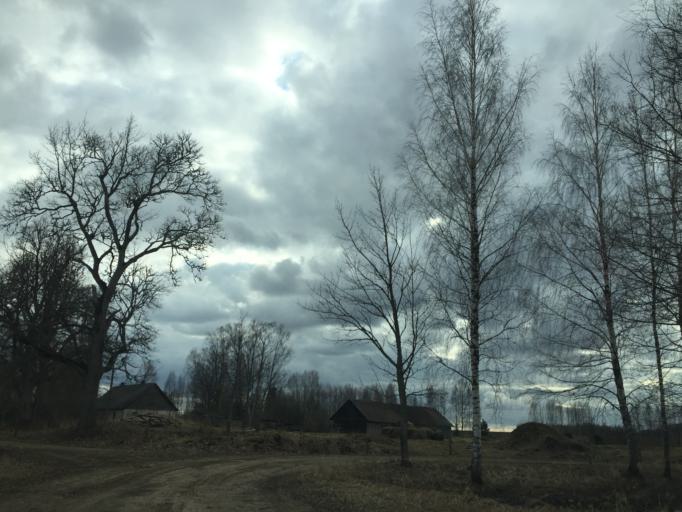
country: LV
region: Lielvarde
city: Lielvarde
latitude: 56.4885
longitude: 24.7799
